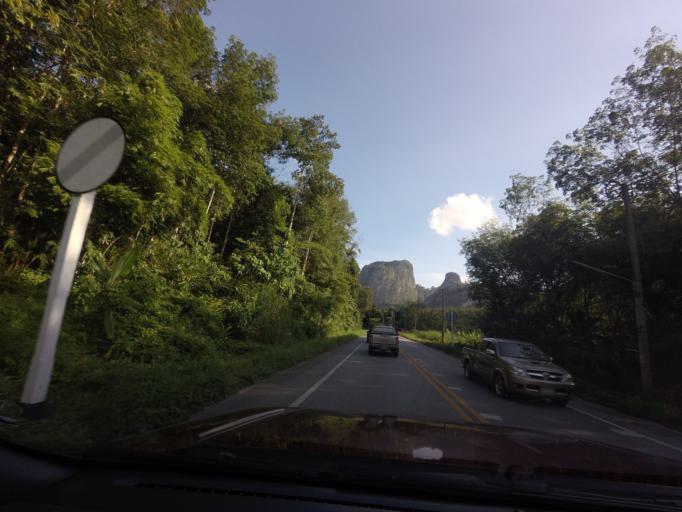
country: TH
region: Yala
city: Than To
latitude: 6.2291
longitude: 101.1663
